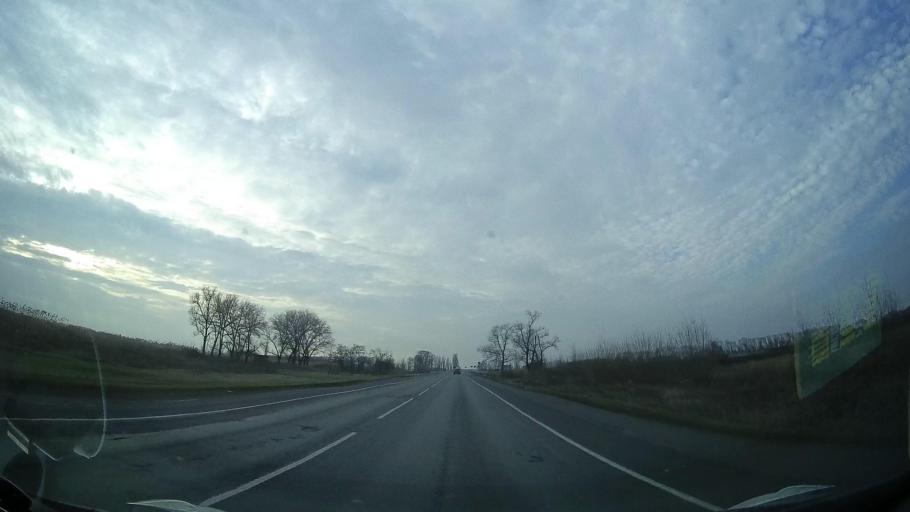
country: RU
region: Rostov
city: Starocherkasskaya
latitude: 47.1548
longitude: 40.1711
